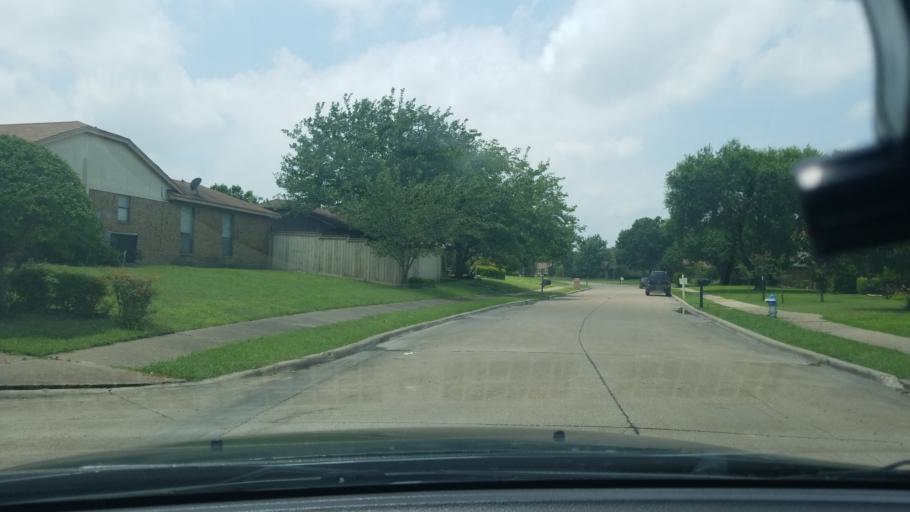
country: US
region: Texas
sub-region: Dallas County
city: Mesquite
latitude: 32.8001
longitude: -96.6119
